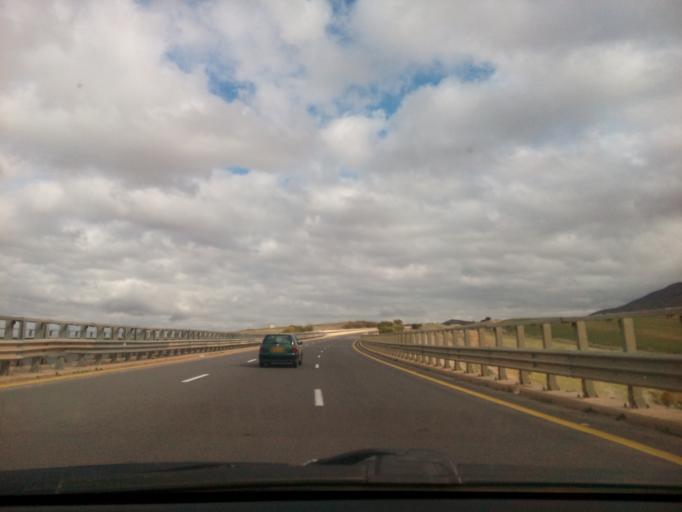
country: DZ
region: Tlemcen
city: Sidi Abdelli
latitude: 35.0077
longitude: -1.1836
